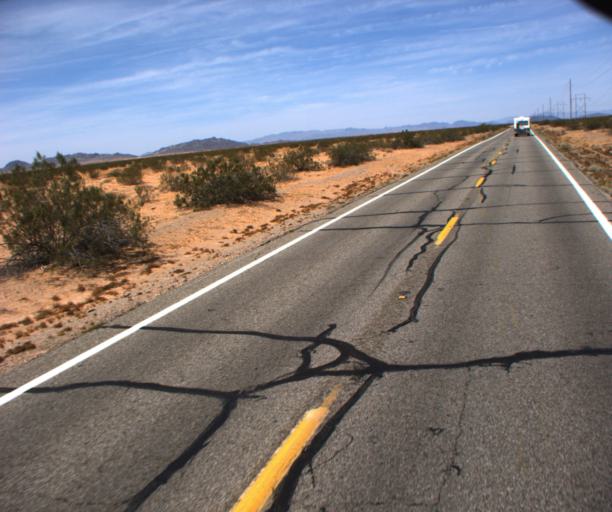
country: US
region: Arizona
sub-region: La Paz County
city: Quartzsite
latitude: 33.8860
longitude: -114.2169
